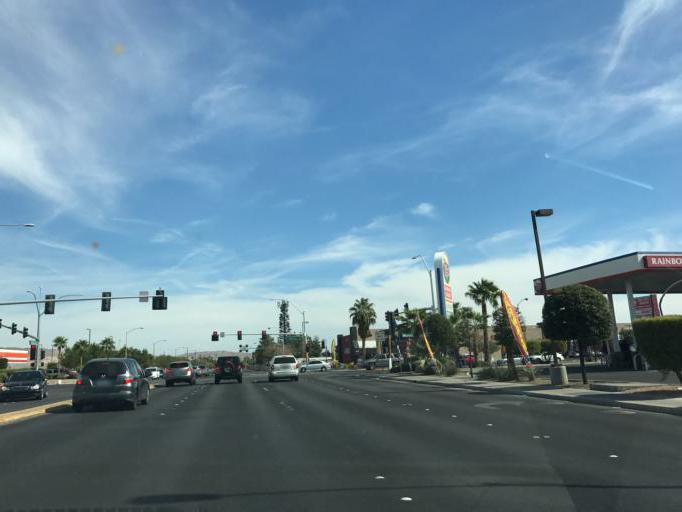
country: US
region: Nevada
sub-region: Clark County
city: Winchester
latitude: 36.1296
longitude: -115.0661
